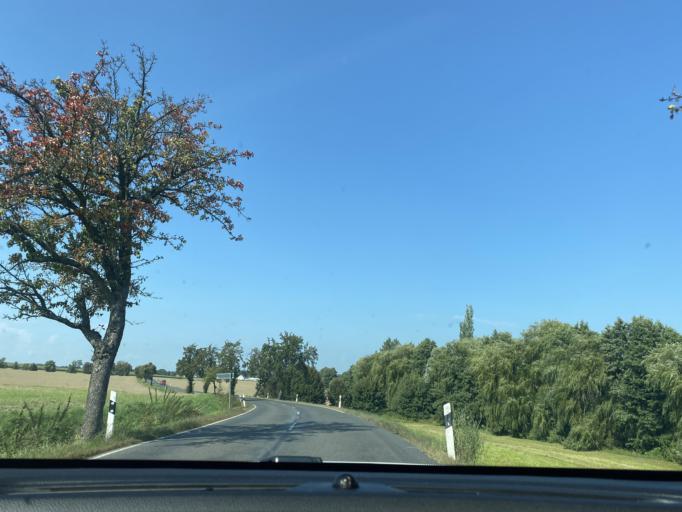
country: DE
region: Saxony
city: Reichenbach
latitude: 51.1788
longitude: 14.7717
